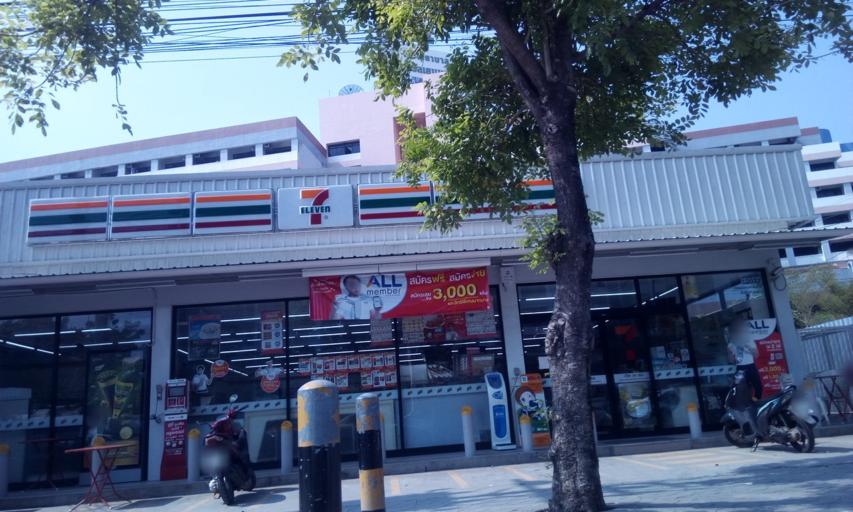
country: TH
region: Bangkok
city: Bang Khen
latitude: 13.8897
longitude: 100.6073
